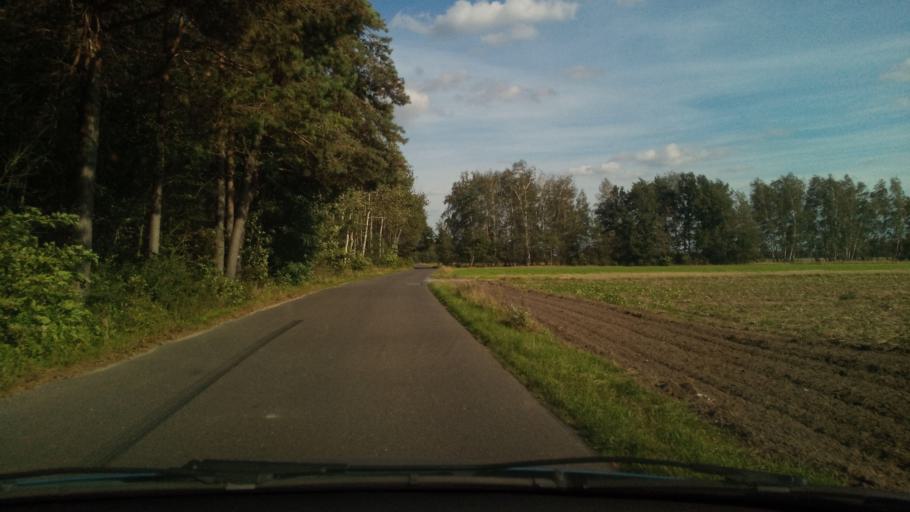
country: PL
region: Lodz Voivodeship
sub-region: Powiat piotrkowski
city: Sulejow
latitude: 51.4093
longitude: 19.8413
